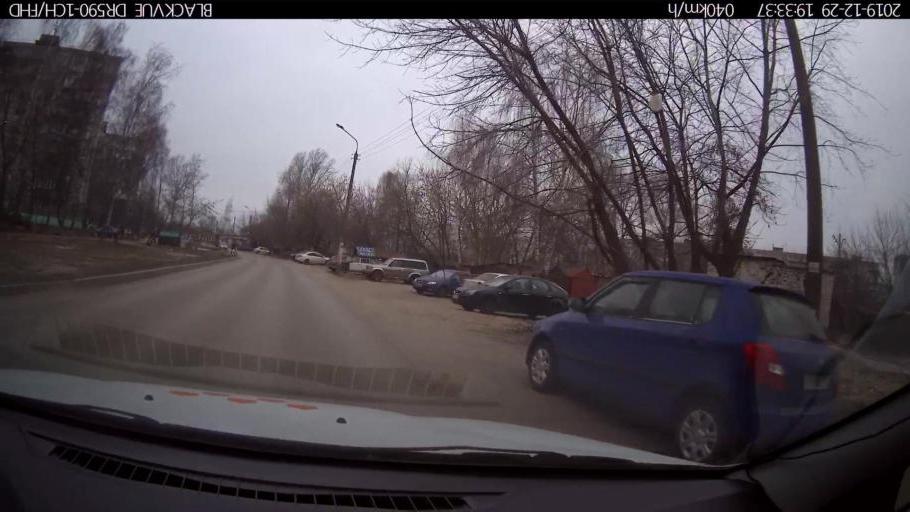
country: RU
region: Nizjnij Novgorod
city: Neklyudovo
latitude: 56.3557
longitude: 43.8606
